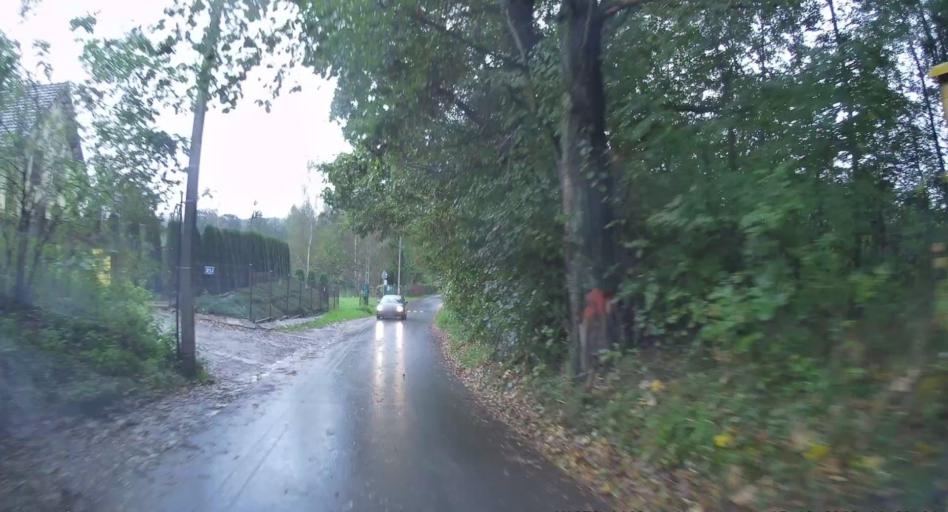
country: PL
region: Lesser Poland Voivodeship
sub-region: Powiat krakowski
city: Ochojno
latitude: 49.9901
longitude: 19.9891
